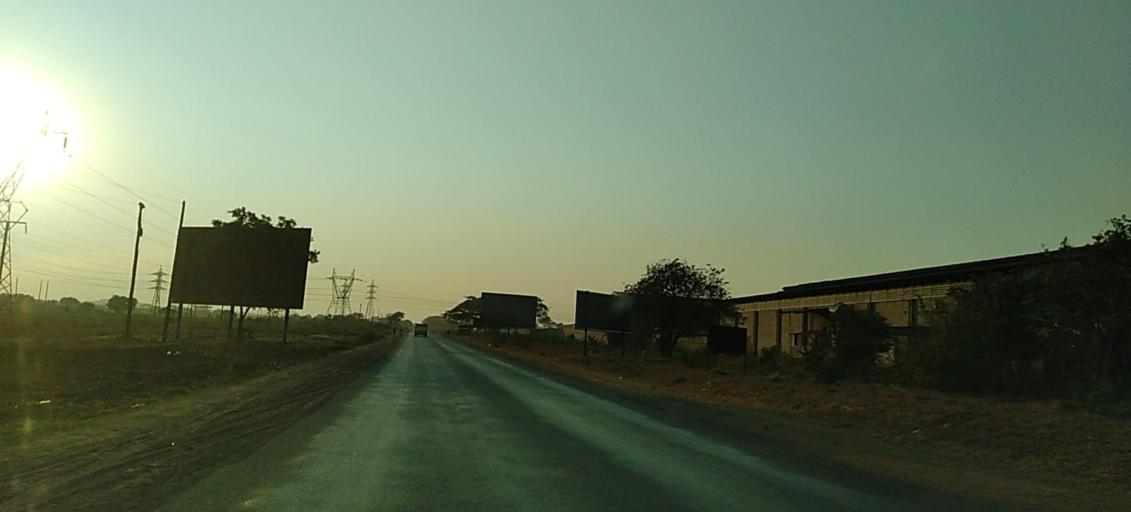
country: ZM
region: Copperbelt
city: Ndola
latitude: -13.0195
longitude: 28.6682
